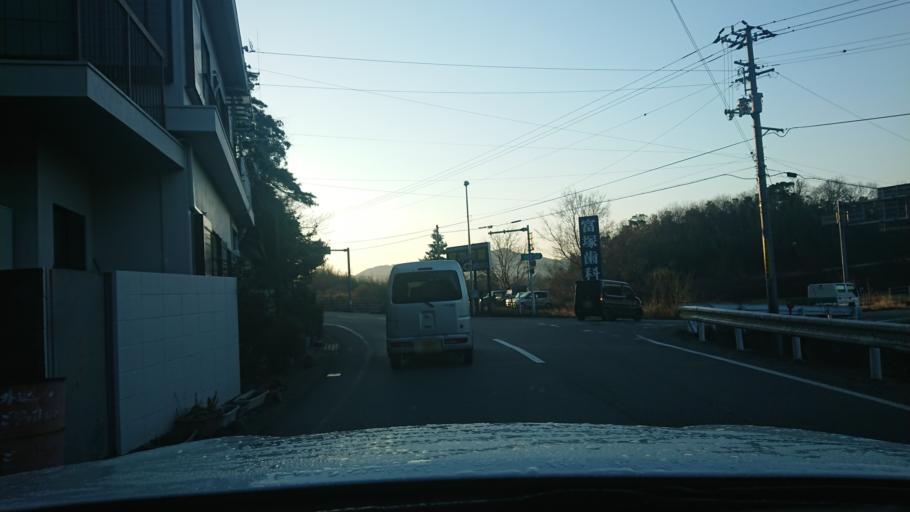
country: JP
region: Tokushima
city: Komatsushimacho
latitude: 33.9442
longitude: 134.5773
